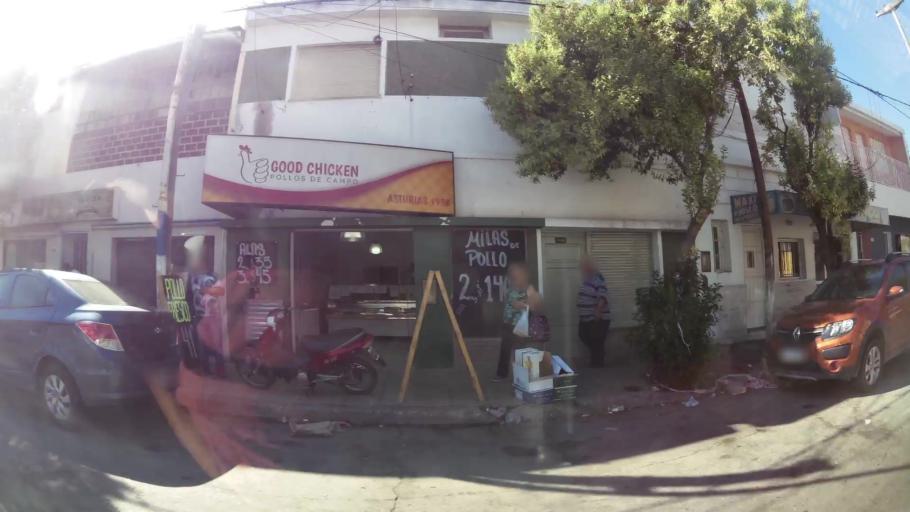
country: AR
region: Cordoba
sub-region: Departamento de Capital
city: Cordoba
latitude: -31.4383
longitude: -64.1573
